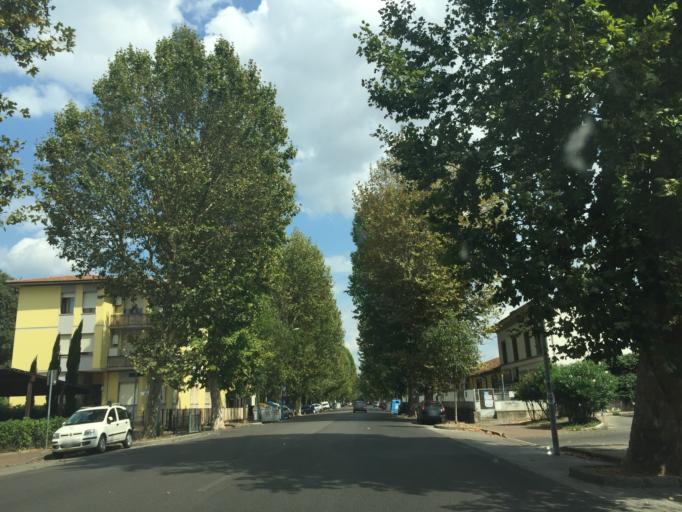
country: IT
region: Tuscany
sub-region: Province of Florence
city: Mantignano-Ugnano
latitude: 43.7941
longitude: 11.1870
